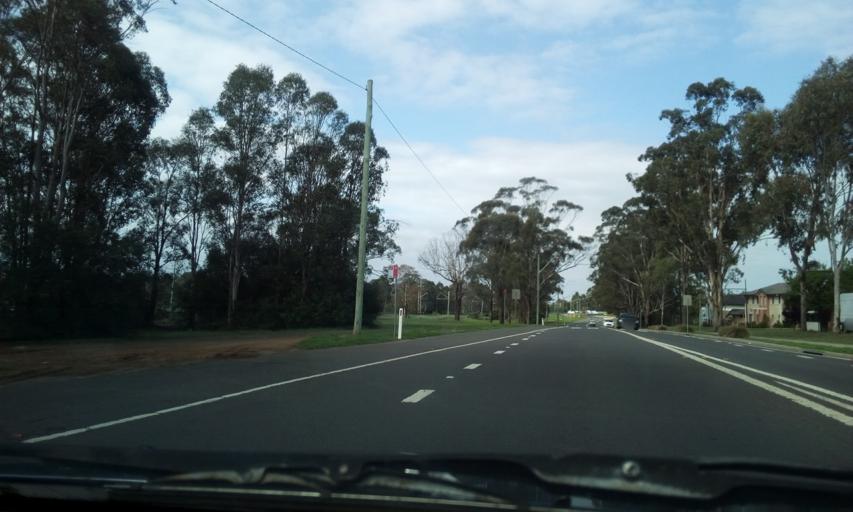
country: AU
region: New South Wales
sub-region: Campbelltown Municipality
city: Glen Alpine
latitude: -34.0743
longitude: 150.7891
